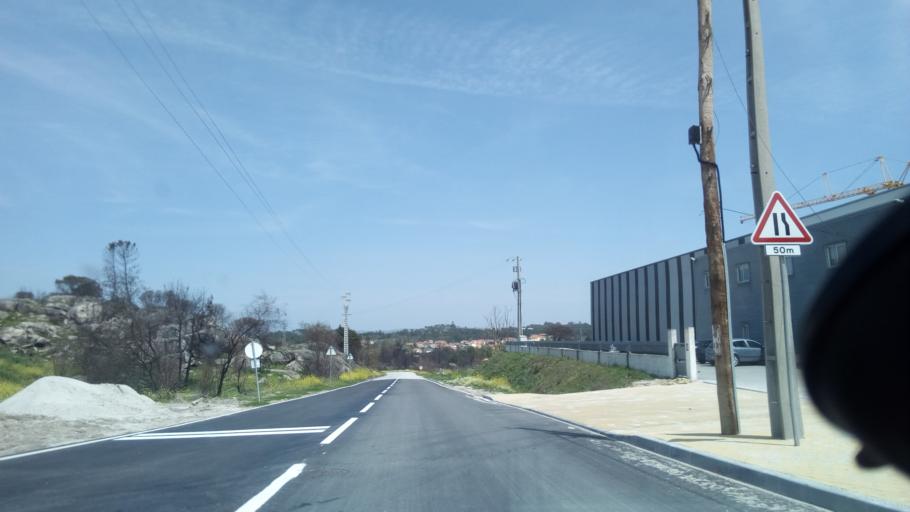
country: PT
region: Viseu
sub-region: Mangualde
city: Mangualde
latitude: 40.6097
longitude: -7.7892
